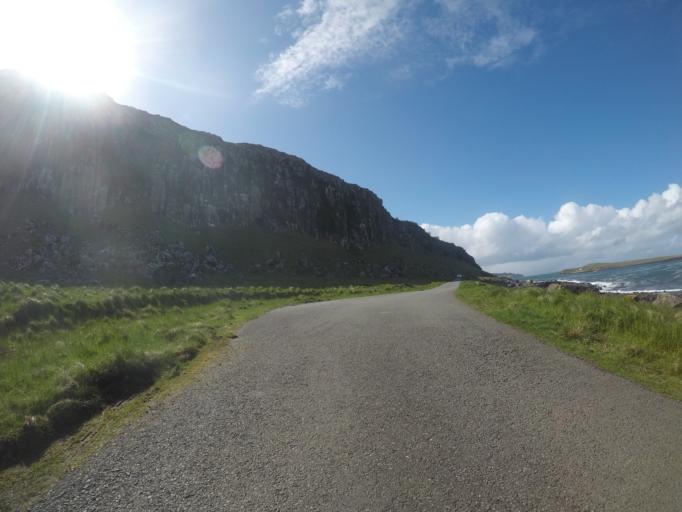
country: GB
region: Scotland
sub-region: Highland
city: Portree
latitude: 57.6332
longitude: -6.1998
